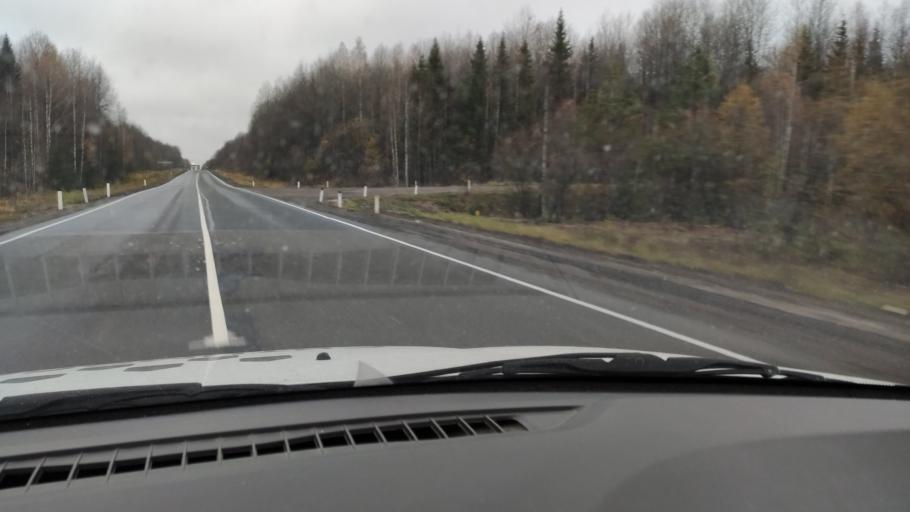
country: RU
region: Kirov
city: Omutninsk
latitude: 58.7558
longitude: 52.0367
